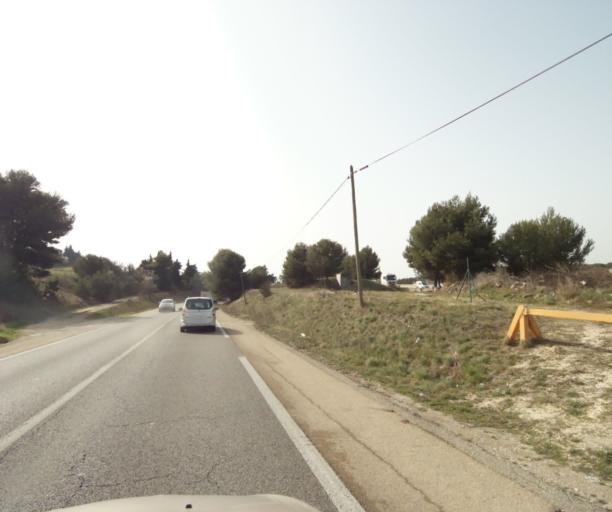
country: FR
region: Provence-Alpes-Cote d'Azur
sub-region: Departement des Bouches-du-Rhone
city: Cabries
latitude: 43.4235
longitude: 5.3748
